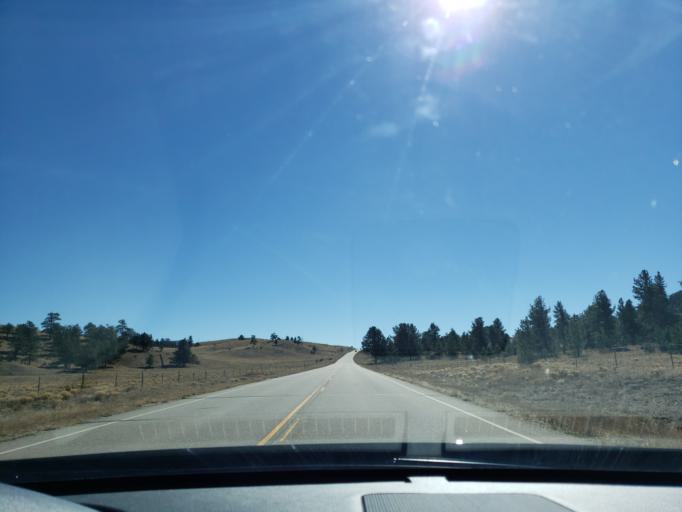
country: US
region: Colorado
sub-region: Park County
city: Fairplay
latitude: 38.9166
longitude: -105.7058
